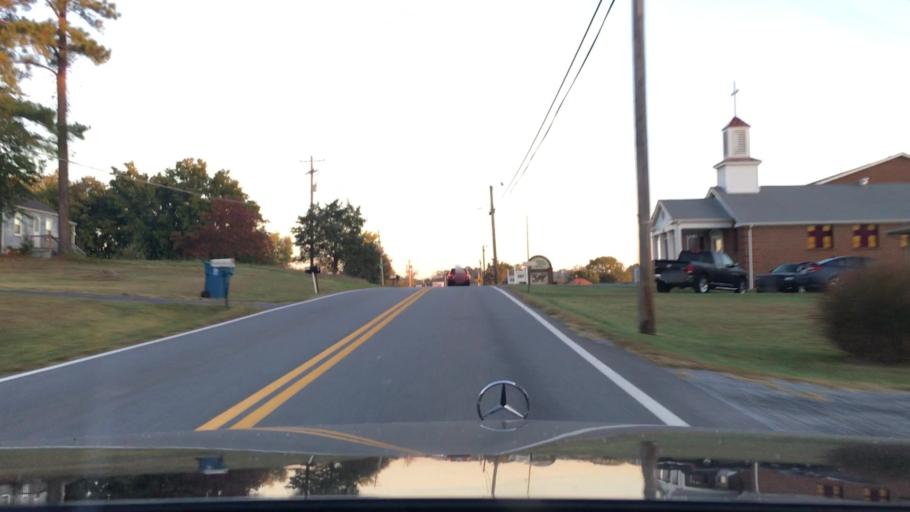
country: US
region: Virginia
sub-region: Campbell County
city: Timberlake
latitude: 37.3086
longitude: -79.2363
